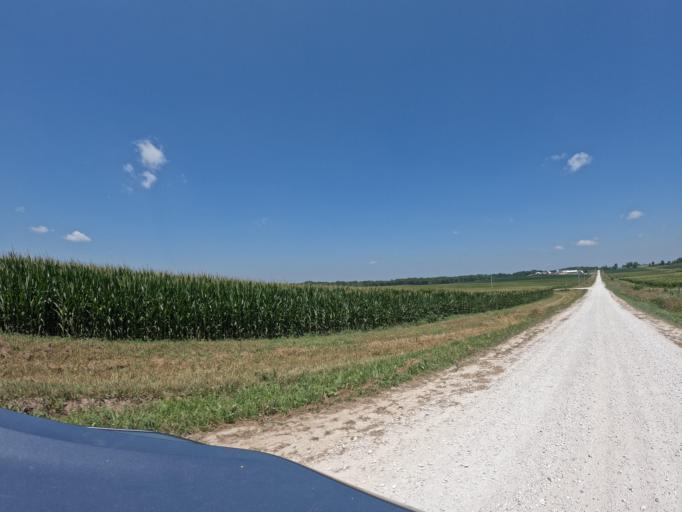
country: US
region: Iowa
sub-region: Keokuk County
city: Sigourney
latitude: 41.2874
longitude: -92.2190
